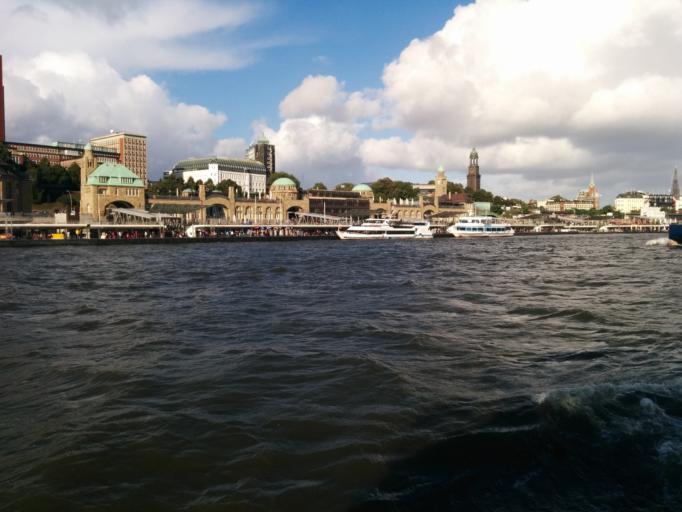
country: DE
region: Hamburg
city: St. Pauli
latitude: 53.5441
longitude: 9.9656
